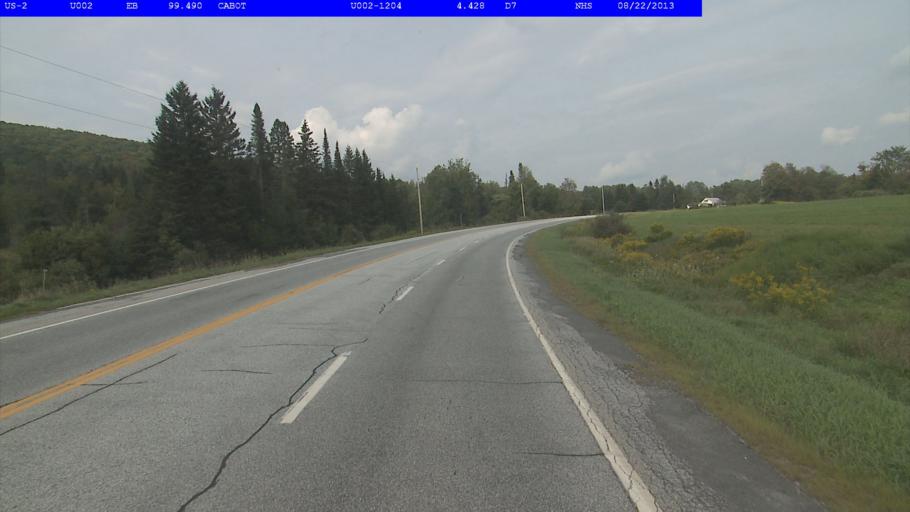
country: US
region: Vermont
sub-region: Caledonia County
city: Hardwick
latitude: 44.3881
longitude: -72.2545
